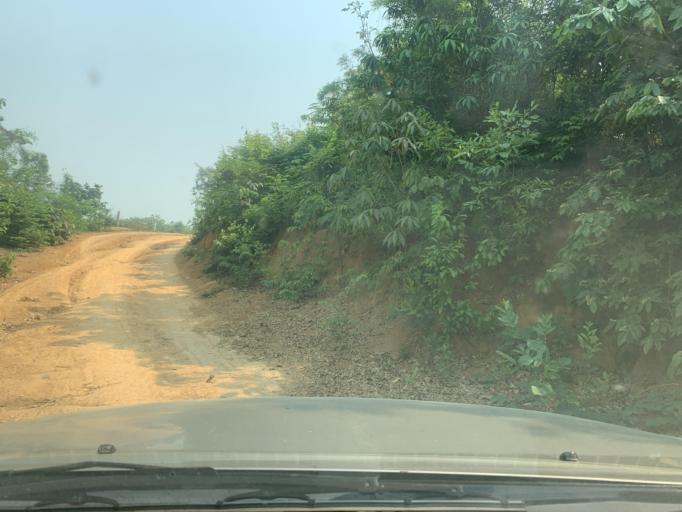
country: LA
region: Louangphabang
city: Xiang Ngeun
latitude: 19.7999
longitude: 102.2022
